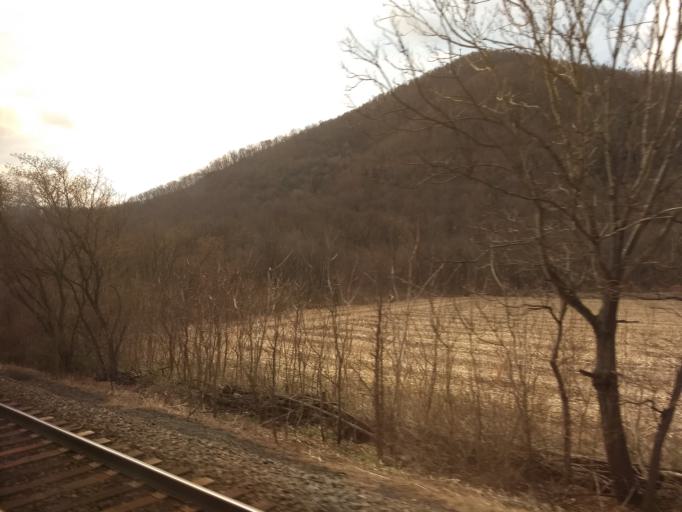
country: US
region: Pennsylvania
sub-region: Huntingdon County
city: Huntingdon
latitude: 40.4476
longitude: -77.9601
